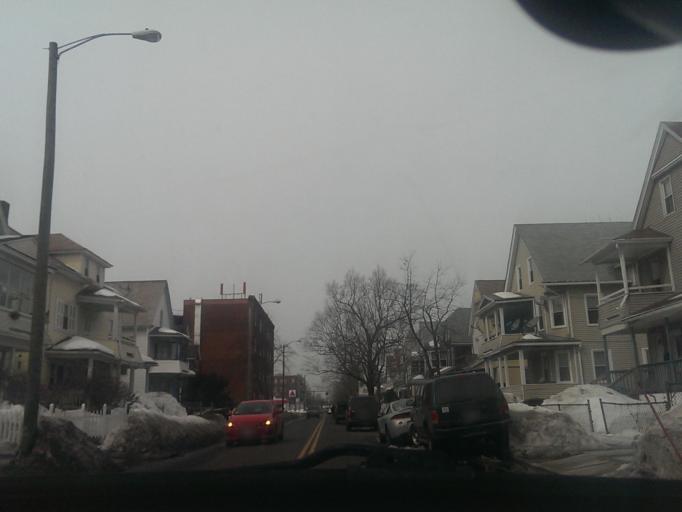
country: US
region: Massachusetts
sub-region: Hampden County
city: Springfield
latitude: 42.0921
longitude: -72.5553
